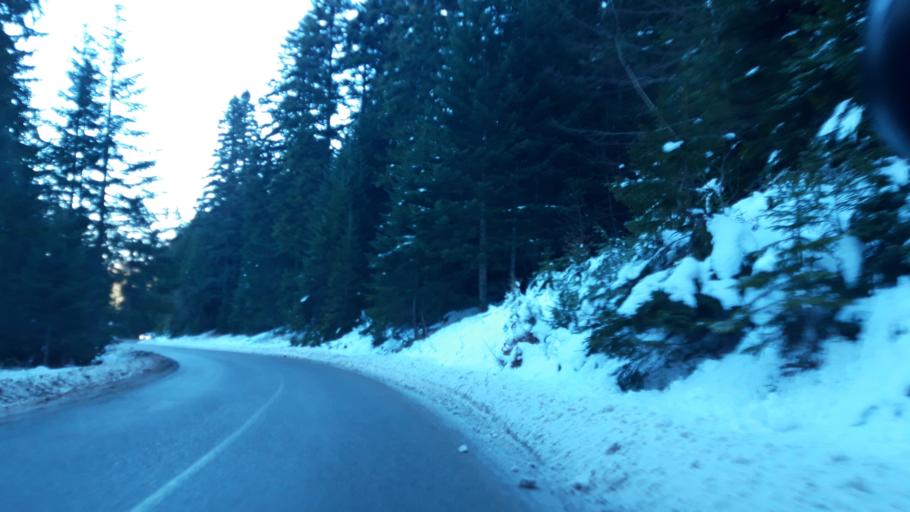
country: BA
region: Republika Srpska
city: Koran
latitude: 43.7727
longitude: 18.5502
